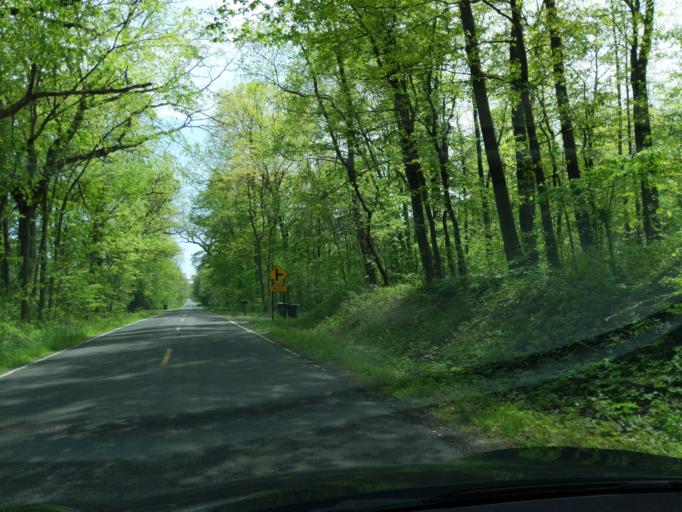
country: US
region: Michigan
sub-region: Ingham County
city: Stockbridge
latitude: 42.4685
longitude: -84.1789
